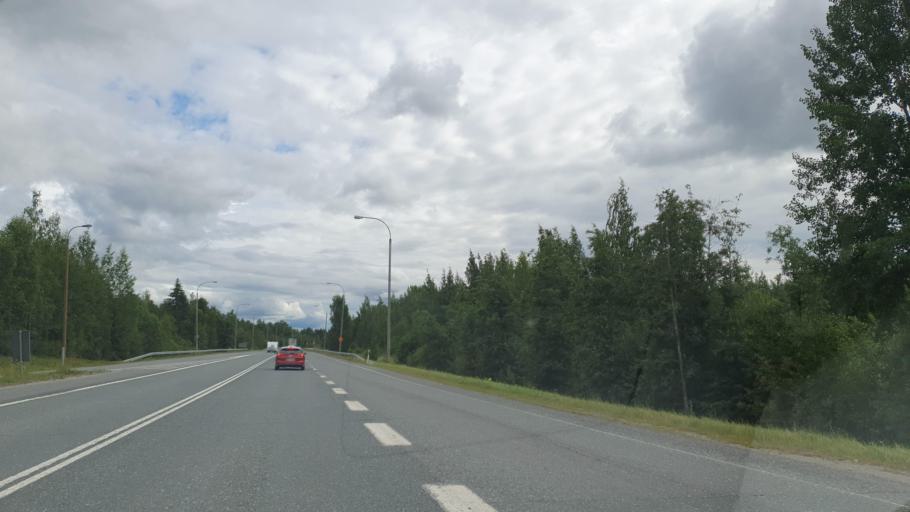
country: FI
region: Northern Savo
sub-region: Ylae-Savo
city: Iisalmi
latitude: 63.5726
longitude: 27.2432
